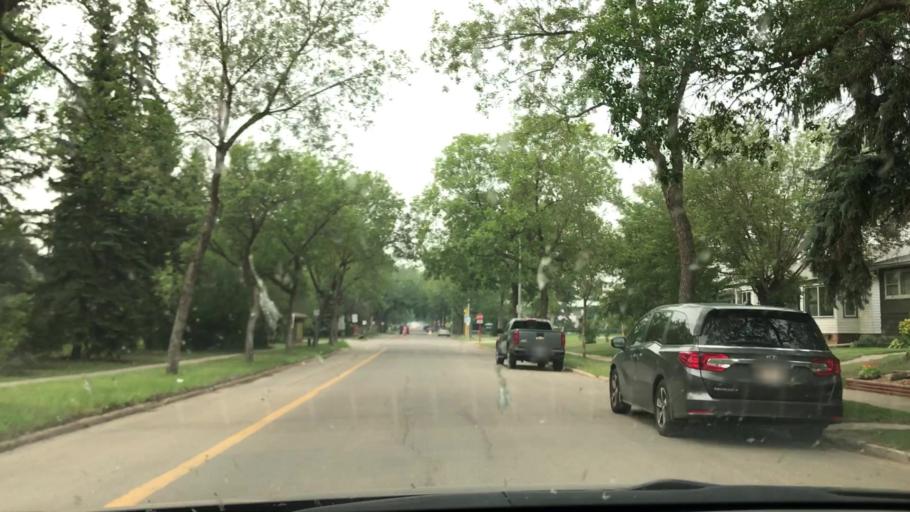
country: CA
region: Alberta
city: Edmonton
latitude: 53.5644
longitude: -113.5412
